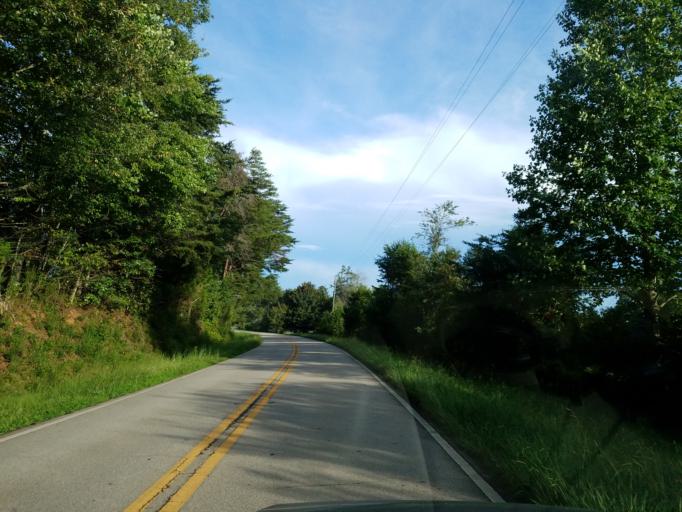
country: US
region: Georgia
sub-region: White County
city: Cleveland
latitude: 34.6133
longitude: -83.8679
